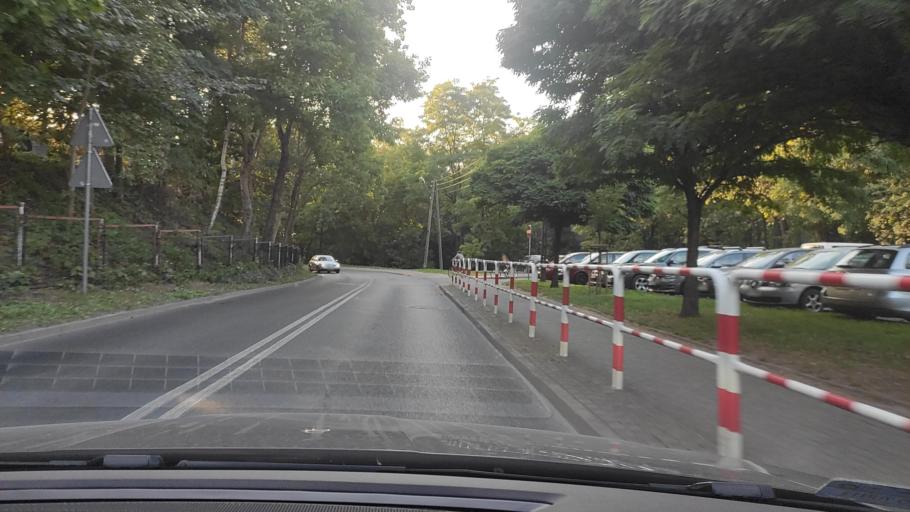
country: PL
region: Greater Poland Voivodeship
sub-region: Powiat poznanski
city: Swarzedz
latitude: 52.4133
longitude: 17.0760
